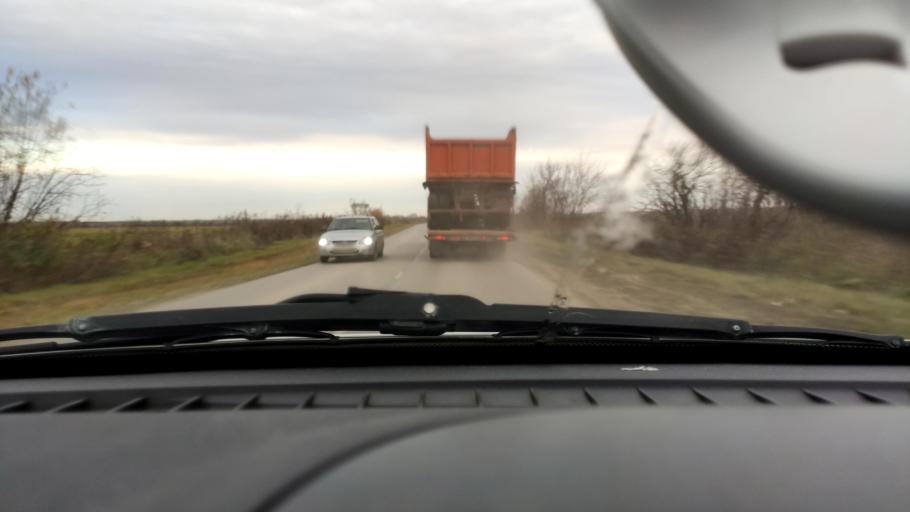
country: RU
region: Perm
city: Kondratovo
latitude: 57.9909
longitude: 56.0937
